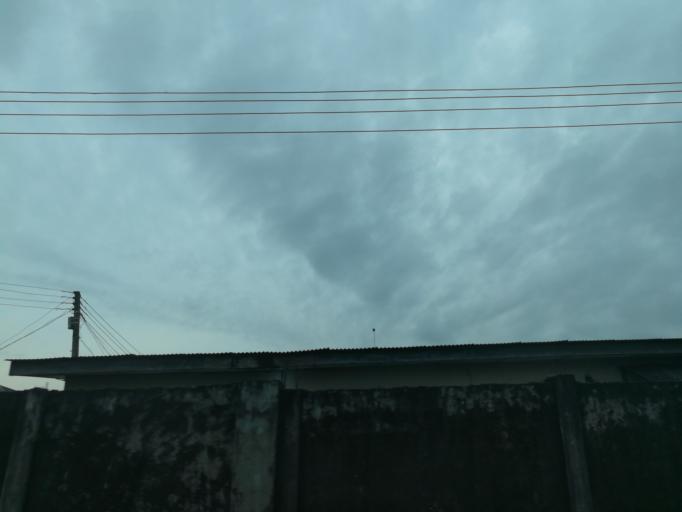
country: NG
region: Rivers
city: Port Harcourt
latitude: 4.8323
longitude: 7.0200
